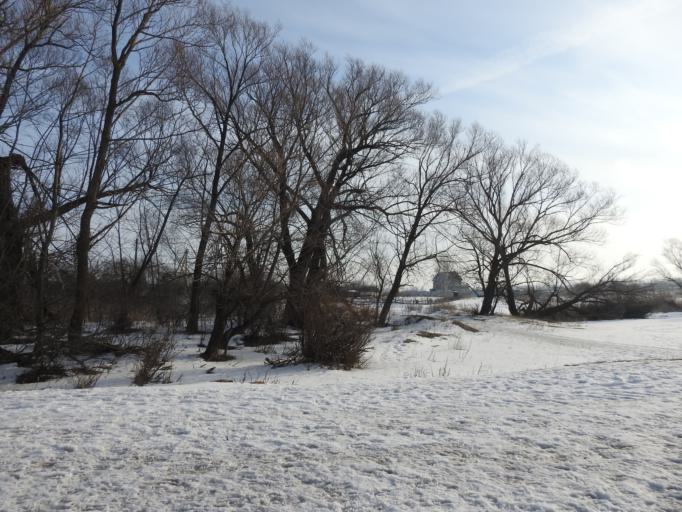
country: RU
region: Saratov
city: Krasnyy Oktyabr'
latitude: 51.4927
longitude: 45.7321
